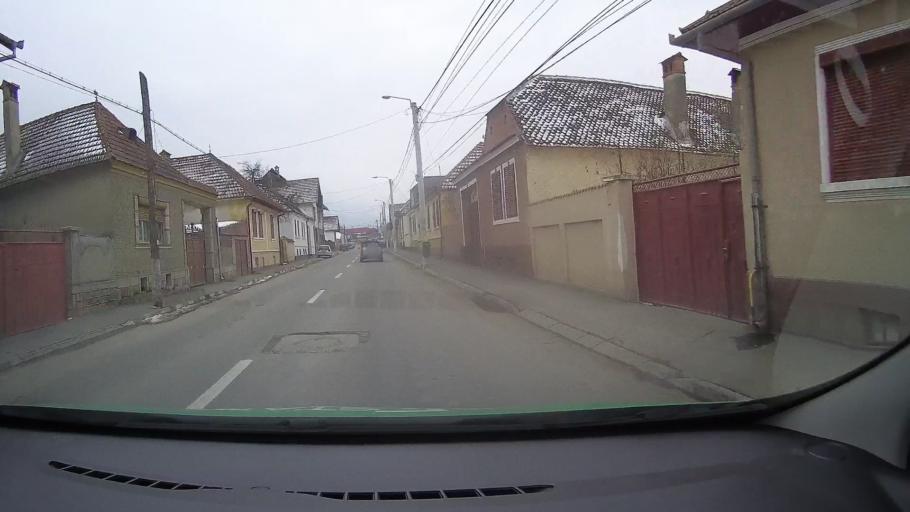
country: RO
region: Brasov
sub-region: Oras Rasnov
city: Rasnov
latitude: 45.5792
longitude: 25.4572
